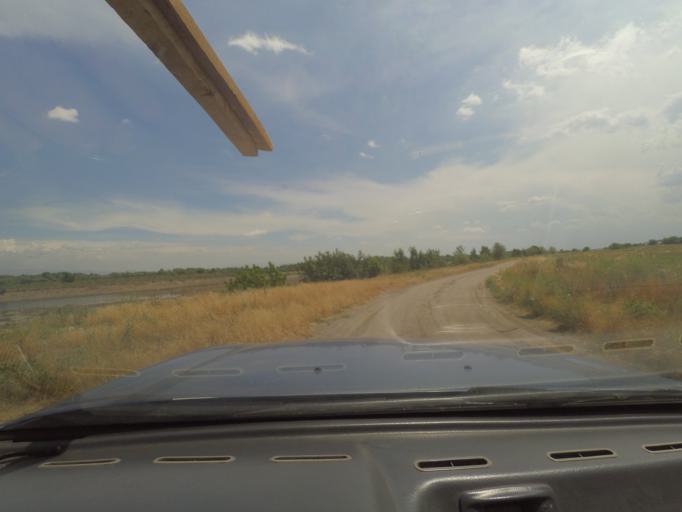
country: TJ
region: Viloyati Sughd
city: Buston
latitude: 40.5450
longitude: 69.0791
